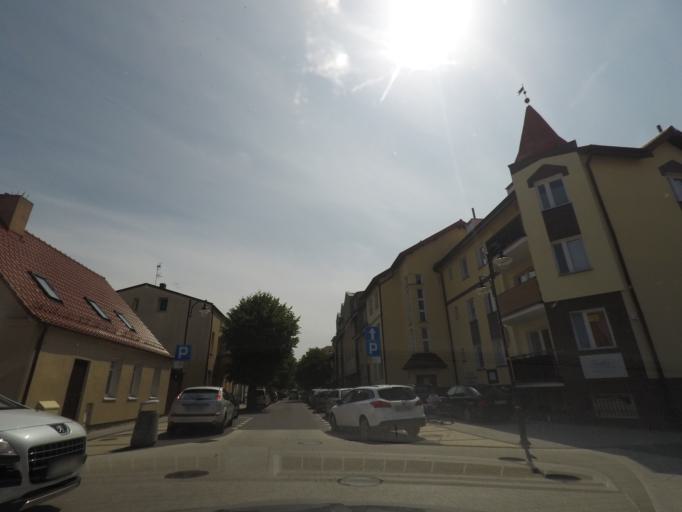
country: PL
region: Pomeranian Voivodeship
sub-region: Powiat slupski
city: Ustka
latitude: 54.5861
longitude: 16.8590
